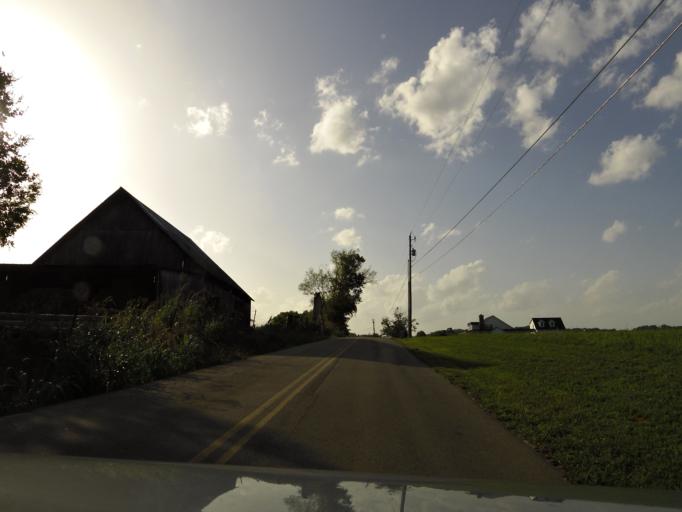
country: US
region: Tennessee
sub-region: Blount County
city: Wildwood
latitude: 35.8232
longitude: -83.8608
